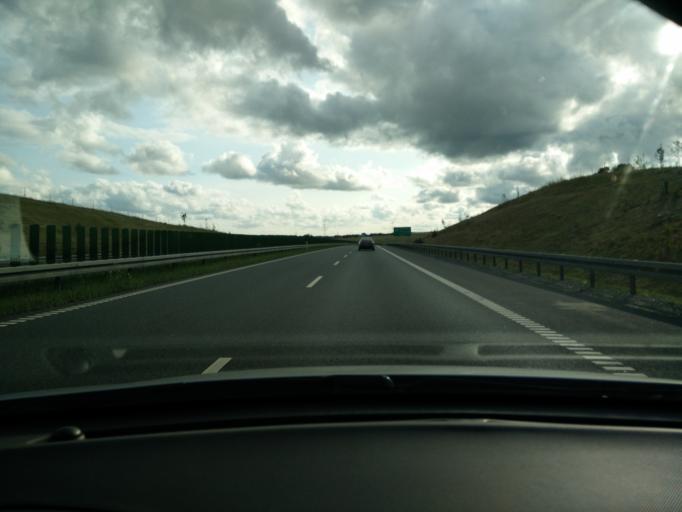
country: PL
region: Pomeranian Voivodeship
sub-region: Powiat gdanski
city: Rotmanka
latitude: 54.2929
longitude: 18.6195
